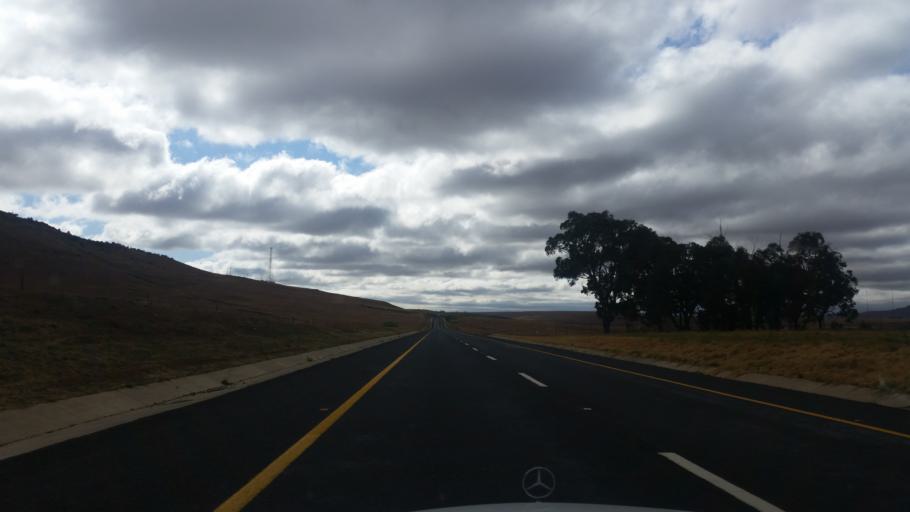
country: ZA
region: Orange Free State
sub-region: Thabo Mofutsanyana District Municipality
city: Phuthaditjhaba
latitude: -28.3124
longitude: 28.7542
